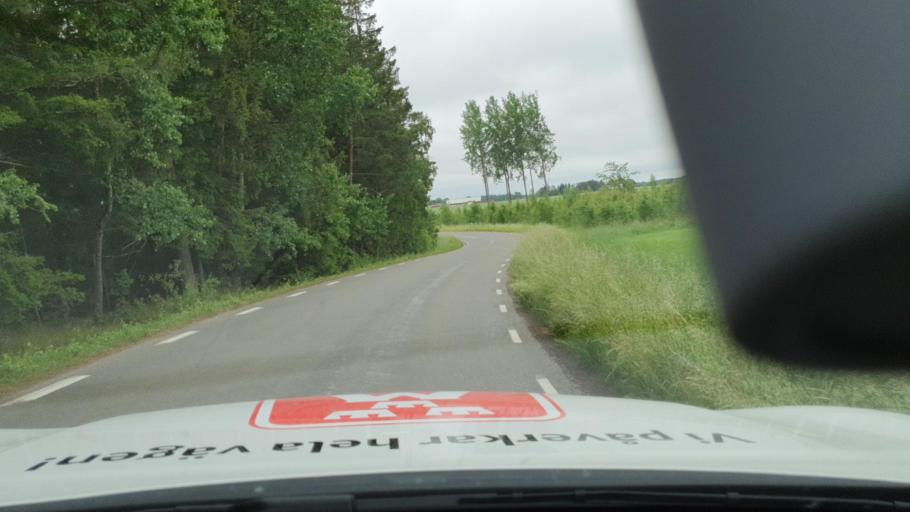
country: SE
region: Vaestra Goetaland
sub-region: Tidaholms Kommun
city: Olofstorp
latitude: 58.3834
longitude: 13.9995
